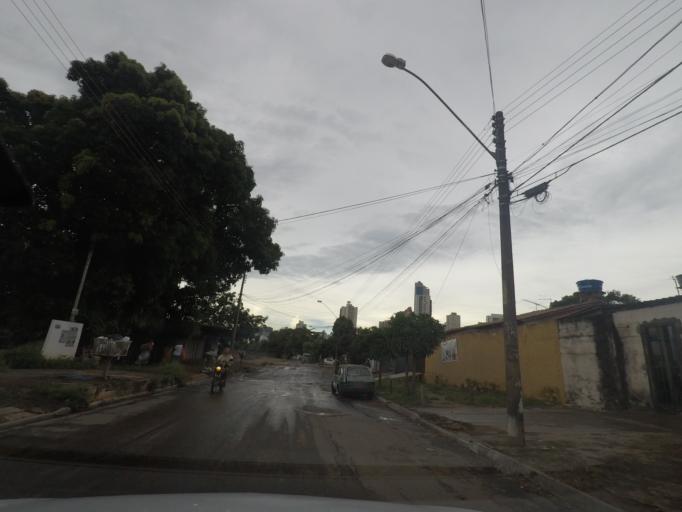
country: BR
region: Goias
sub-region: Goiania
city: Goiania
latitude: -16.7175
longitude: -49.2451
